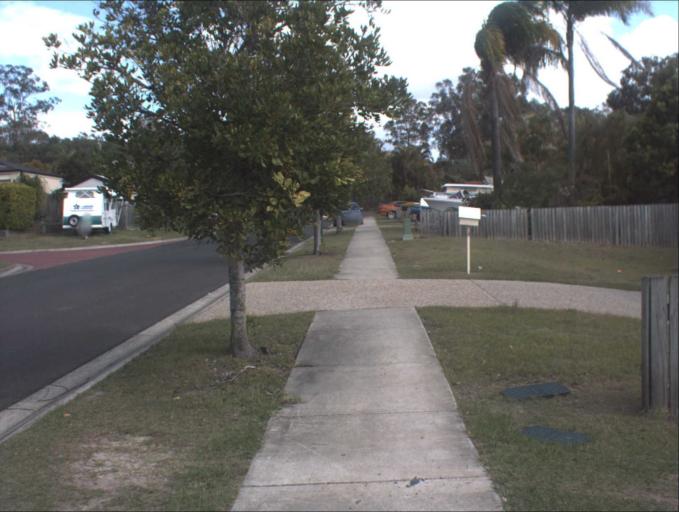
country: AU
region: Queensland
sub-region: Logan
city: Park Ridge South
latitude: -27.6885
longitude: 153.0514
